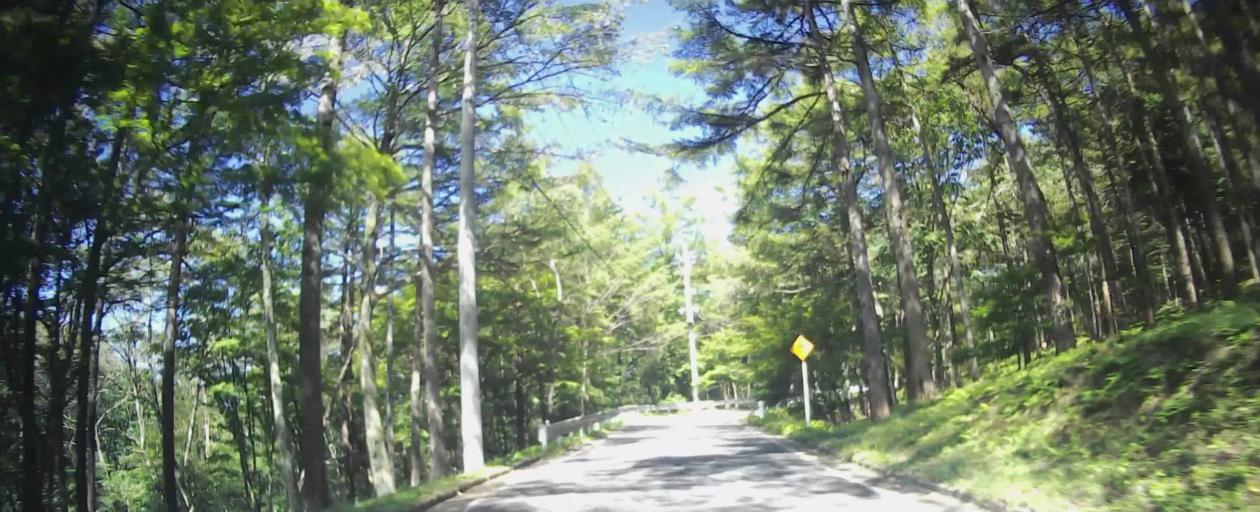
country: JP
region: Gunma
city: Nakanojomachi
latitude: 36.4752
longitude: 138.8721
